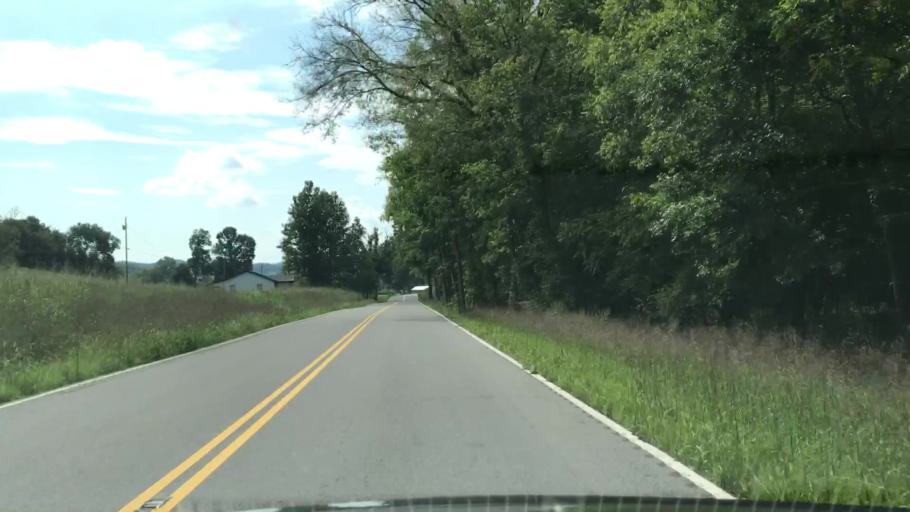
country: US
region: Tennessee
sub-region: Trousdale County
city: Hartsville
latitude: 36.4819
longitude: -86.1869
